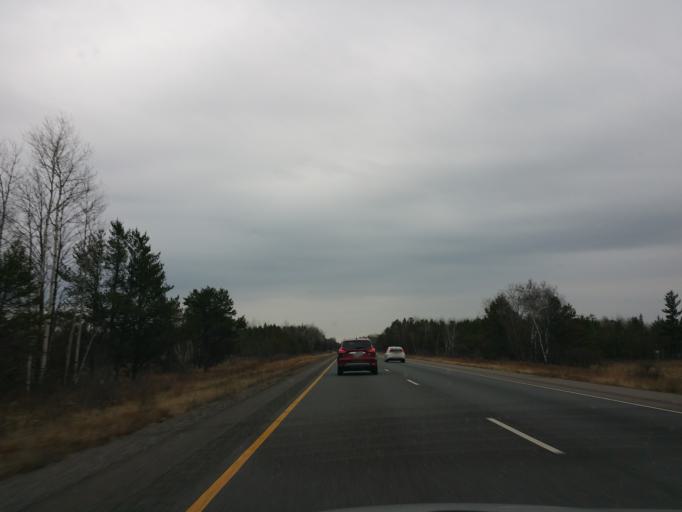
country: US
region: Wisconsin
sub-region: Jackson County
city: Black River Falls
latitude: 44.2647
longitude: -90.7769
